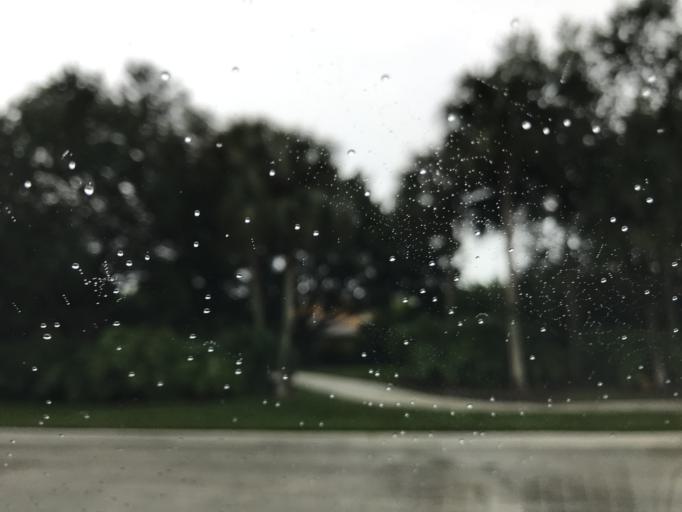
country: US
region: Florida
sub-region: Broward County
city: Coral Springs
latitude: 26.3071
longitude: -80.2857
